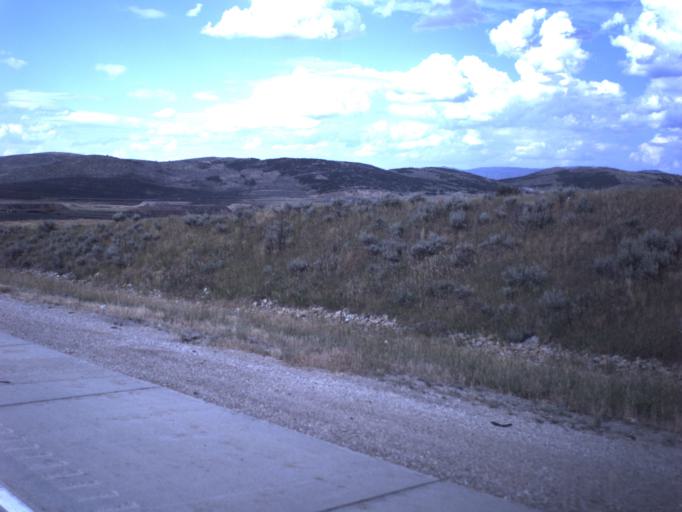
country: US
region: Utah
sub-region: Summit County
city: Park City
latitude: 40.6625
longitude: -111.4584
